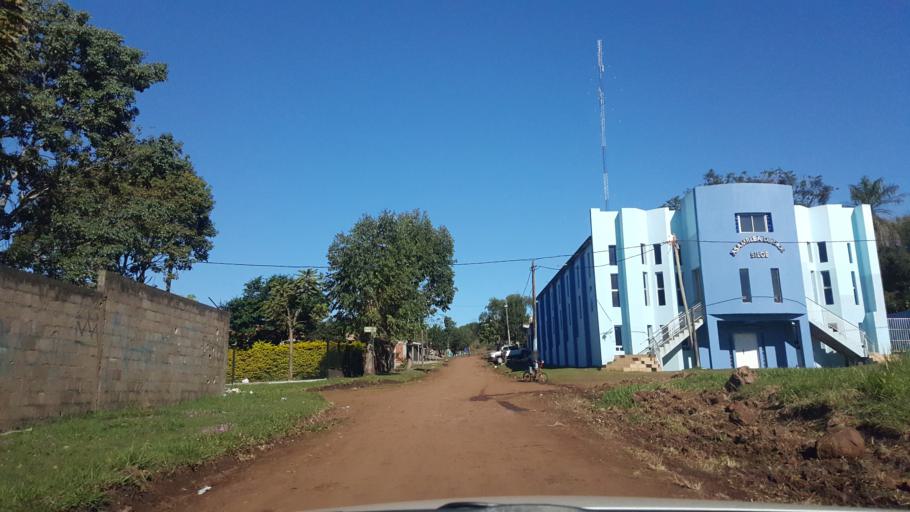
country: AR
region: Misiones
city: Garupa
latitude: -27.4620
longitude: -55.8396
